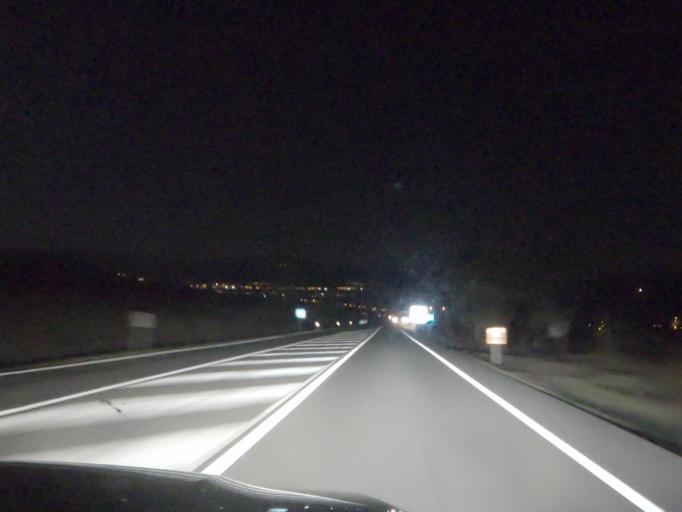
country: ES
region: Galicia
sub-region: Provincia de Ourense
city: Cualedro
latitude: 41.9787
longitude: -7.5237
